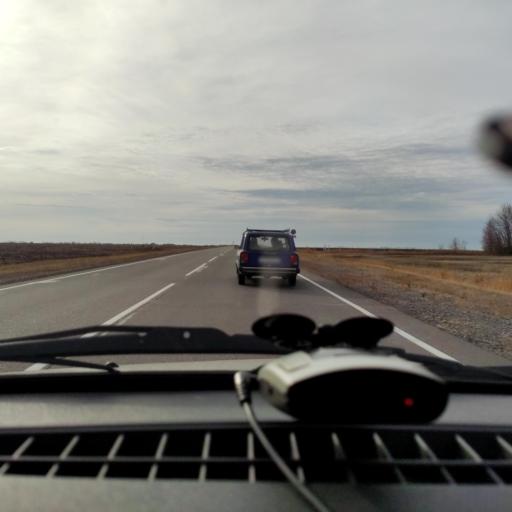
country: RU
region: Voronezj
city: Strelitsa
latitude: 51.4766
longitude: 38.9609
